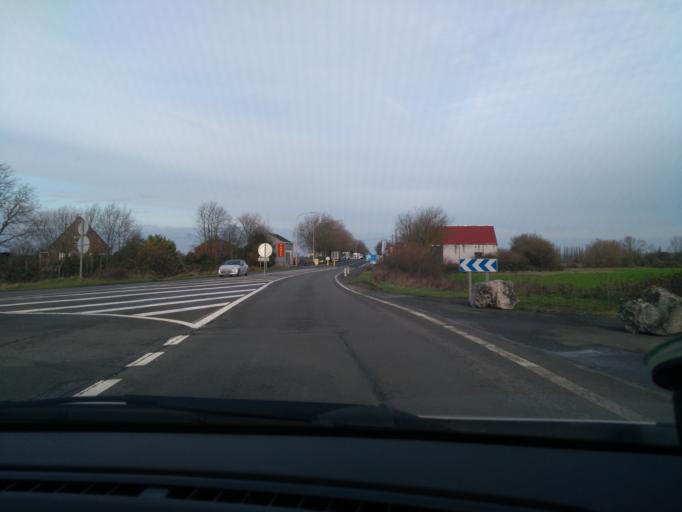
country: BE
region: Wallonia
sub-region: Province du Hainaut
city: Quevy-le-Petit
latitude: 50.3424
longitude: 3.9711
